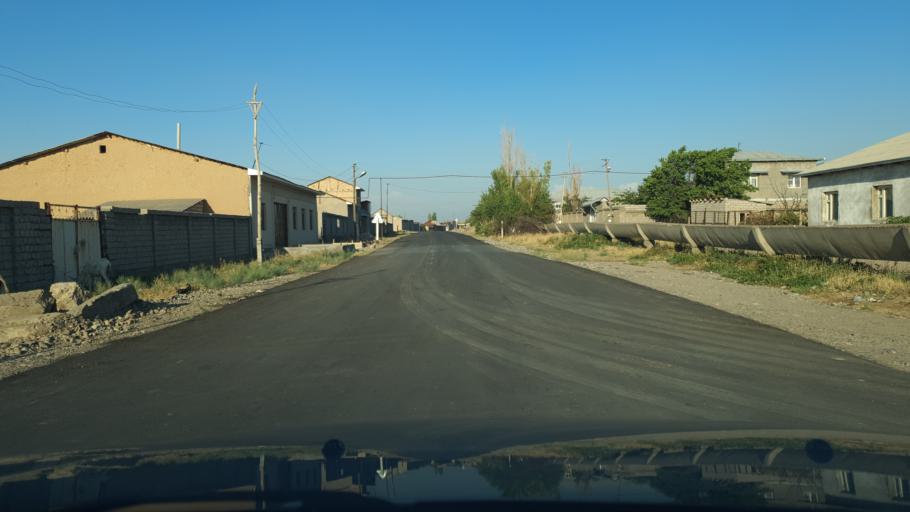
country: UZ
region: Toshkent
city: Salor
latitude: 41.4566
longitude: 69.3983
